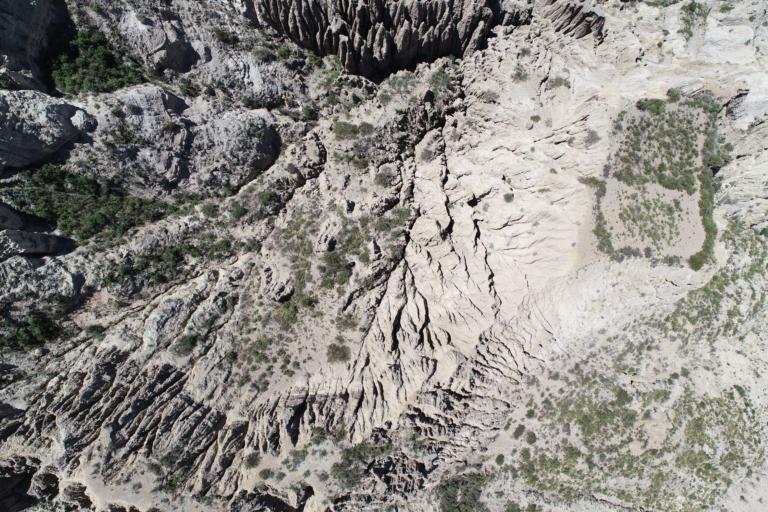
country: BO
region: La Paz
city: La Paz
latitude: -16.5155
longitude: -68.1013
